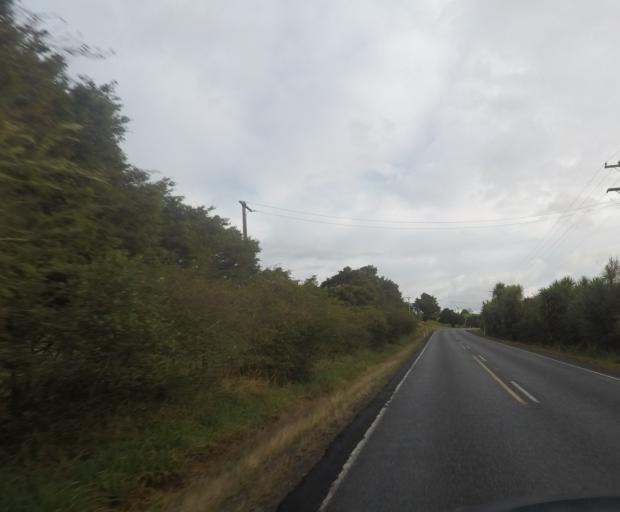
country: NZ
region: Auckland
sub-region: Auckland
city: Wellsford
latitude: -36.2122
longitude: 174.5851
